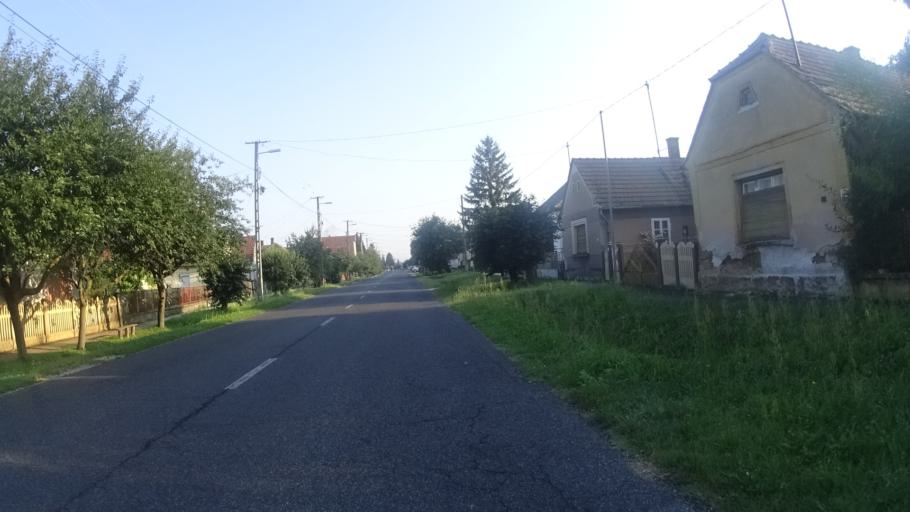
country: HU
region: Zala
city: Zalakomar
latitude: 46.5920
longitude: 17.1763
